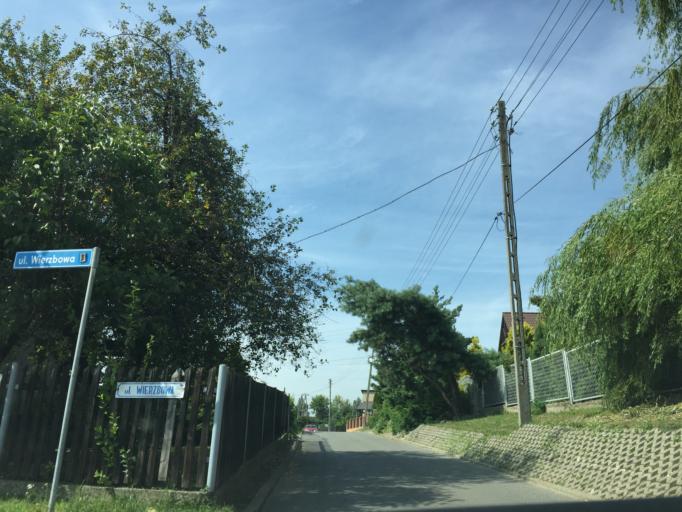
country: PL
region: Silesian Voivodeship
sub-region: Powiat wodzislawski
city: Gorzyce
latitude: 49.9607
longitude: 18.3974
